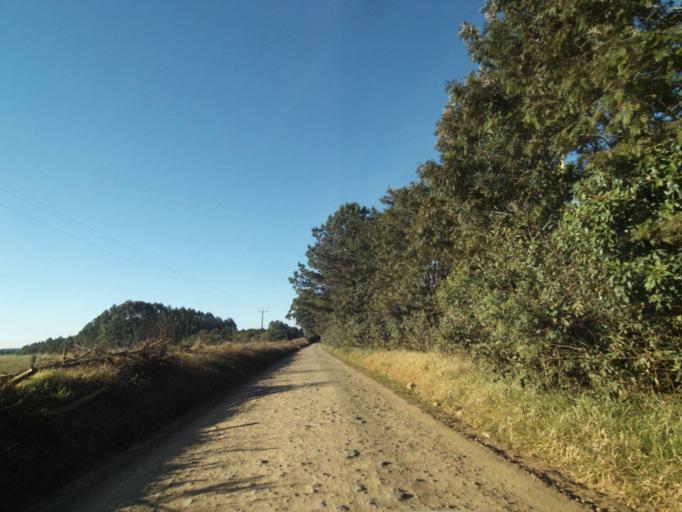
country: BR
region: Parana
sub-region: Tibagi
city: Tibagi
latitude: -24.5449
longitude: -50.6169
